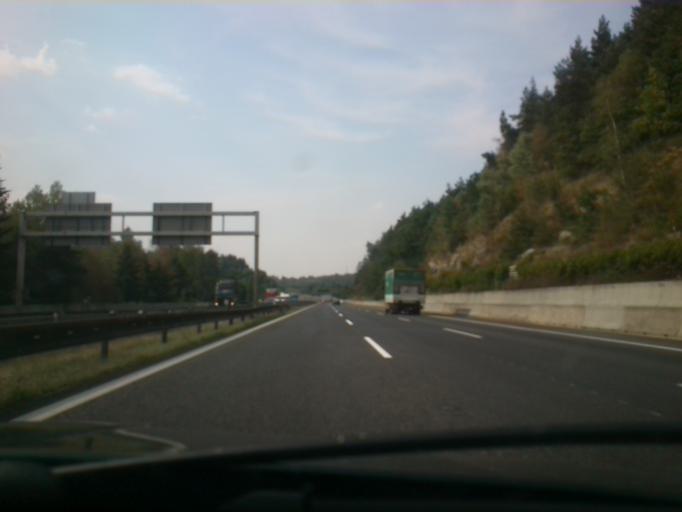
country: CZ
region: Central Bohemia
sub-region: Okres Praha-Vychod
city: Mnichovice
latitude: 49.9211
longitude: 14.7049
